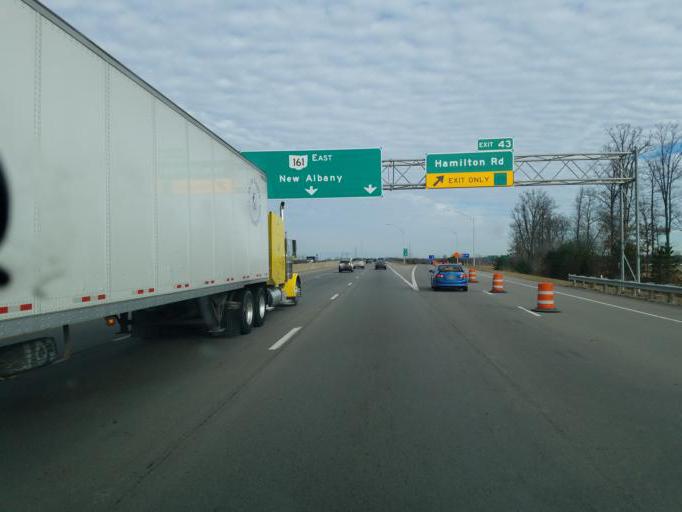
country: US
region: Ohio
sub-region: Franklin County
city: New Albany
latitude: 40.0818
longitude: -82.8594
